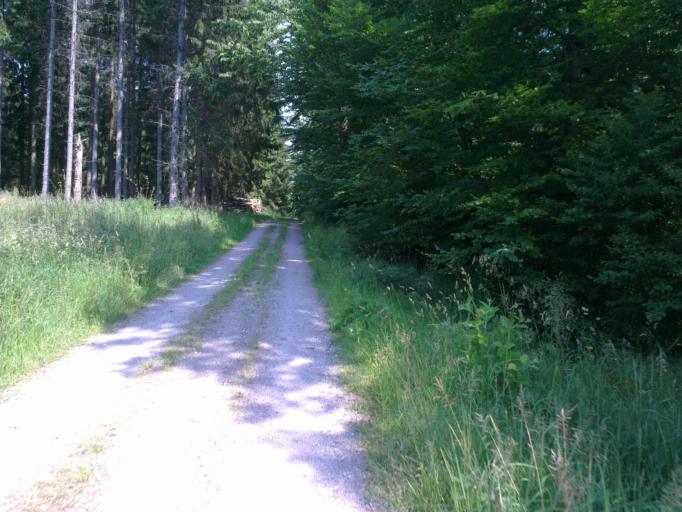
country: DK
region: Capital Region
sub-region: Hillerod Kommune
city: Nodebo
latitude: 55.9291
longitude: 12.3630
